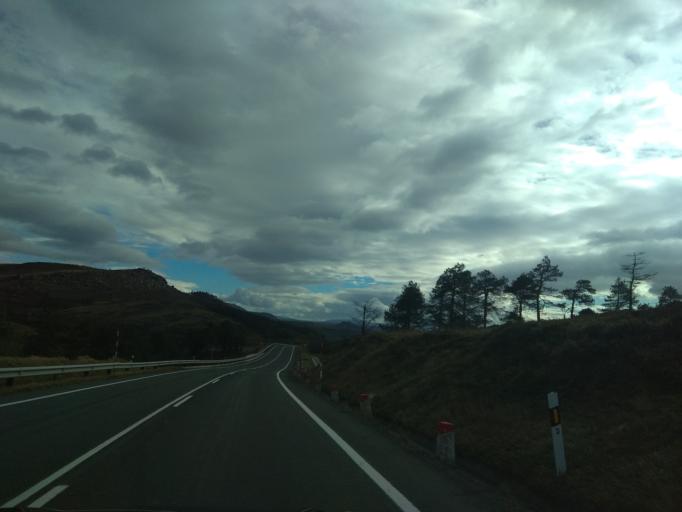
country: ES
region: Castille and Leon
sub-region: Provincia de Burgos
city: Arija
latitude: 43.0382
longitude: -3.8703
